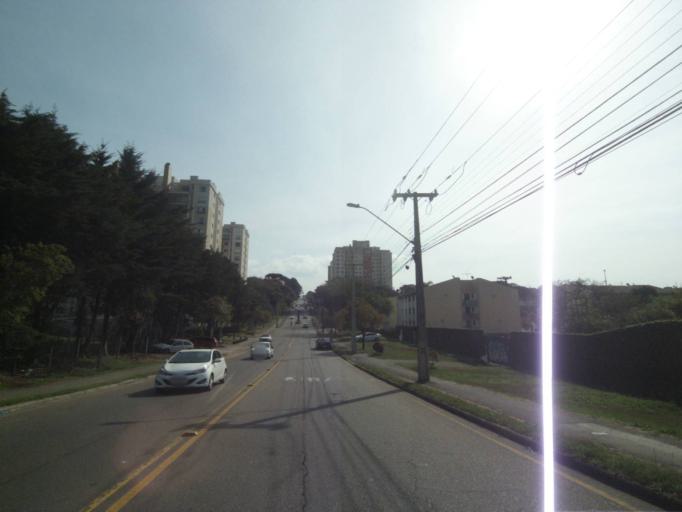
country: BR
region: Parana
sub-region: Curitiba
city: Curitiba
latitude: -25.4596
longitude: -49.3191
